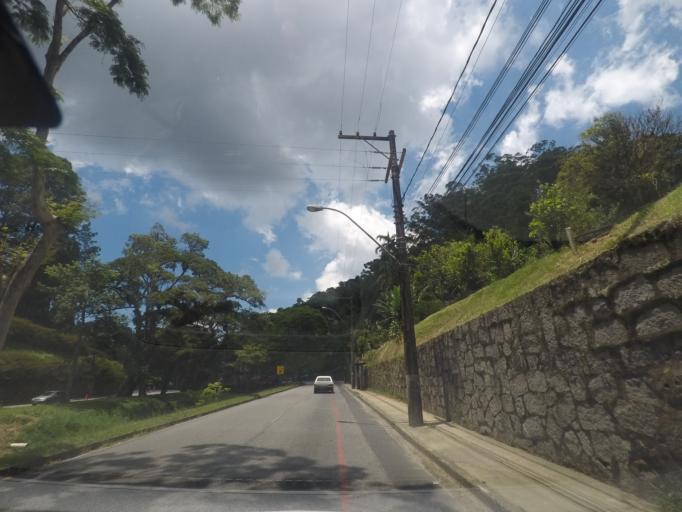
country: BR
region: Rio de Janeiro
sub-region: Petropolis
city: Petropolis
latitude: -22.4968
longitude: -43.1804
